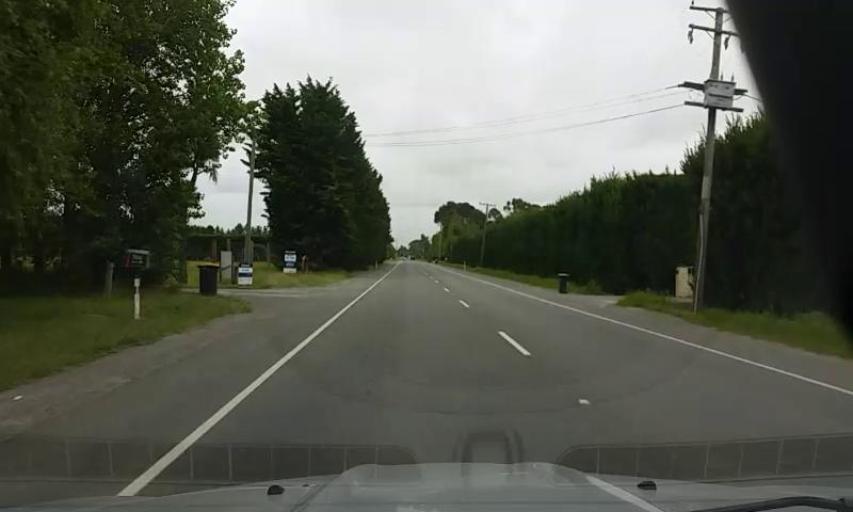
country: NZ
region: Canterbury
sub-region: Selwyn District
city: Prebbleton
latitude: -43.5153
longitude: 172.5176
